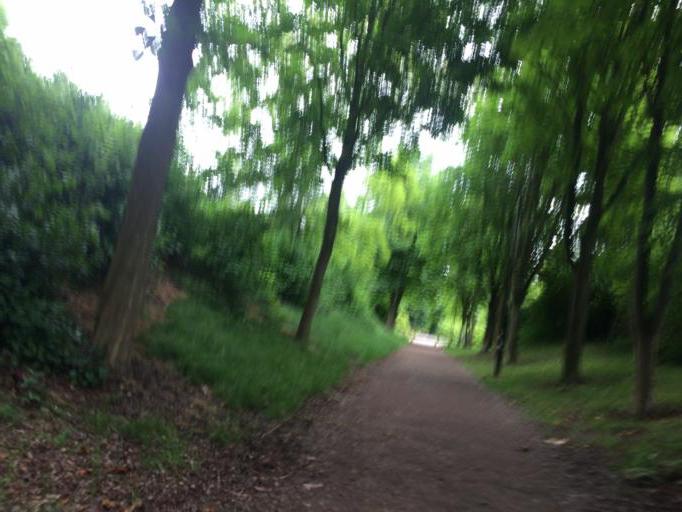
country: GB
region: England
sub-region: Milton Keynes
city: Milton Keynes
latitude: 52.0380
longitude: -0.7512
